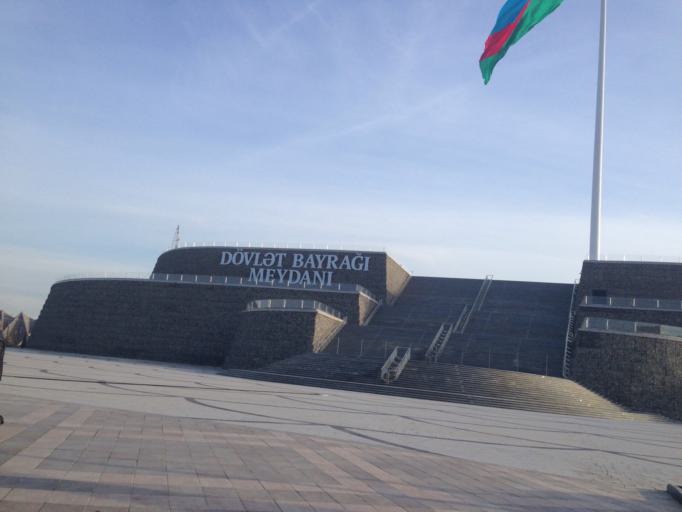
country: AZ
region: Baki
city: Badamdar
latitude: 40.3461
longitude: 49.8438
